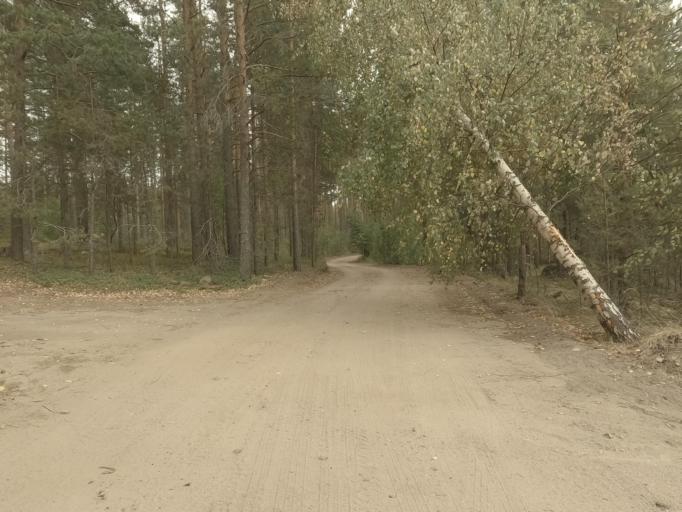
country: RU
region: Leningrad
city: Kamennogorsk
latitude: 60.9950
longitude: 29.1861
